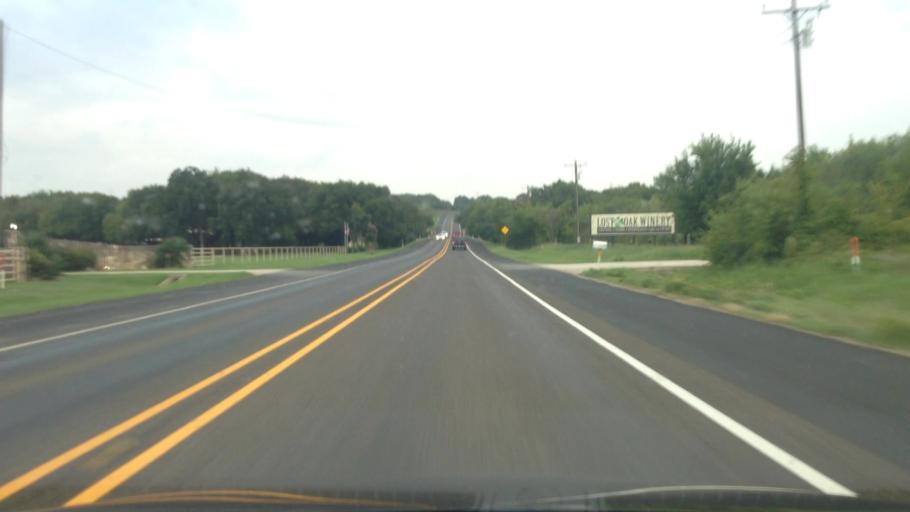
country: US
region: Texas
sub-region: Johnson County
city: Burleson
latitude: 32.5017
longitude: -97.3420
